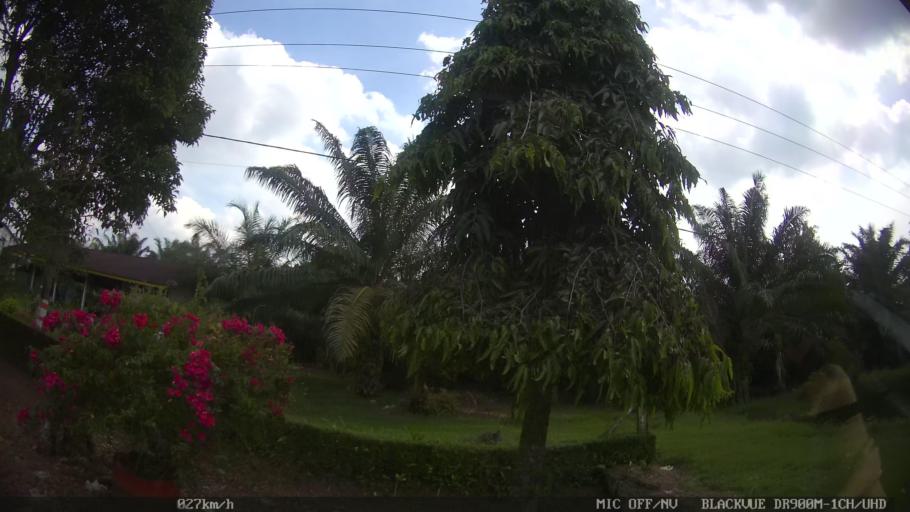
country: ID
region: North Sumatra
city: Binjai
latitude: 3.6354
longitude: 98.5151
